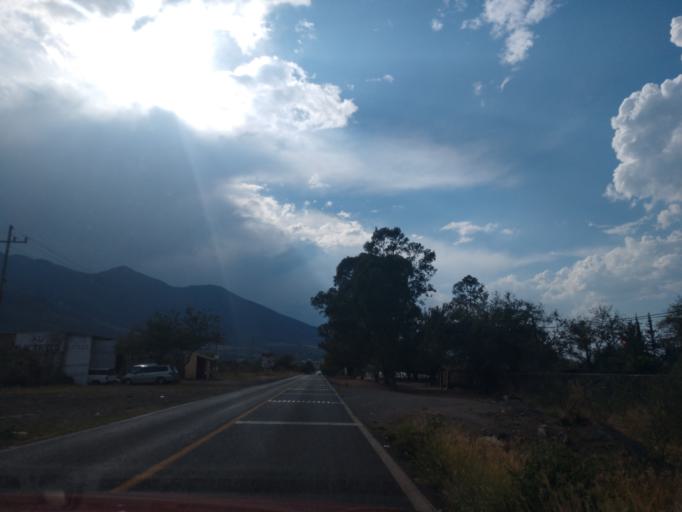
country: MX
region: Jalisco
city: San Juan Cosala
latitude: 20.1938
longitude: -103.2921
